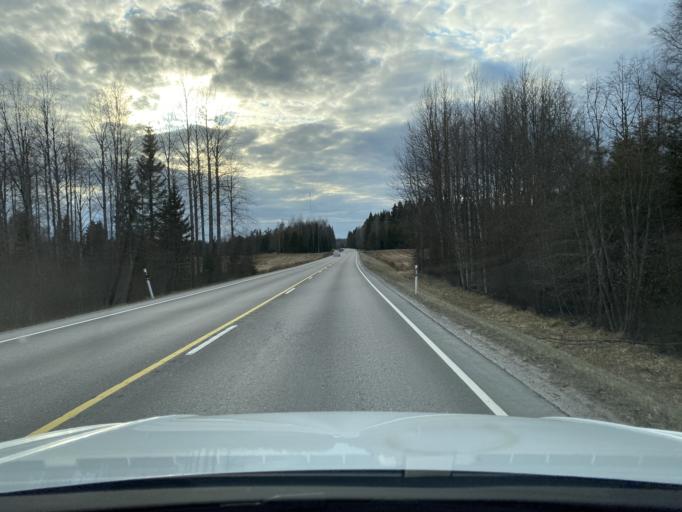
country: FI
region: Haeme
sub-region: Haemeenlinna
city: Renko
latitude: 60.7839
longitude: 24.1515
